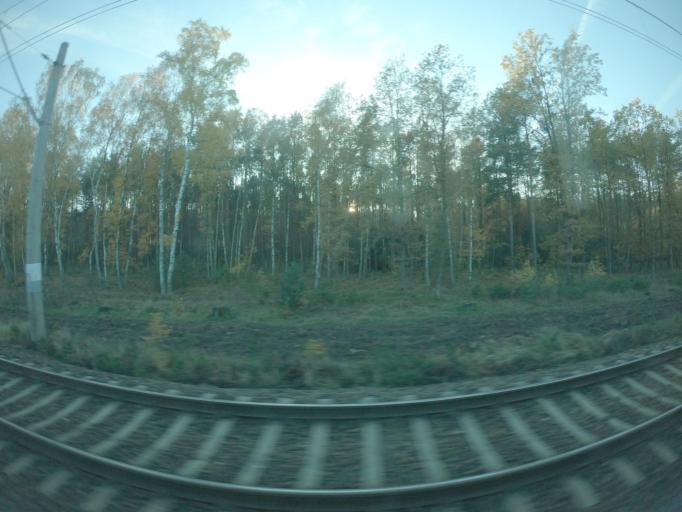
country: PL
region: Lubusz
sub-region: Powiat slubicki
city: Rzepin
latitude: 52.2839
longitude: 14.8994
